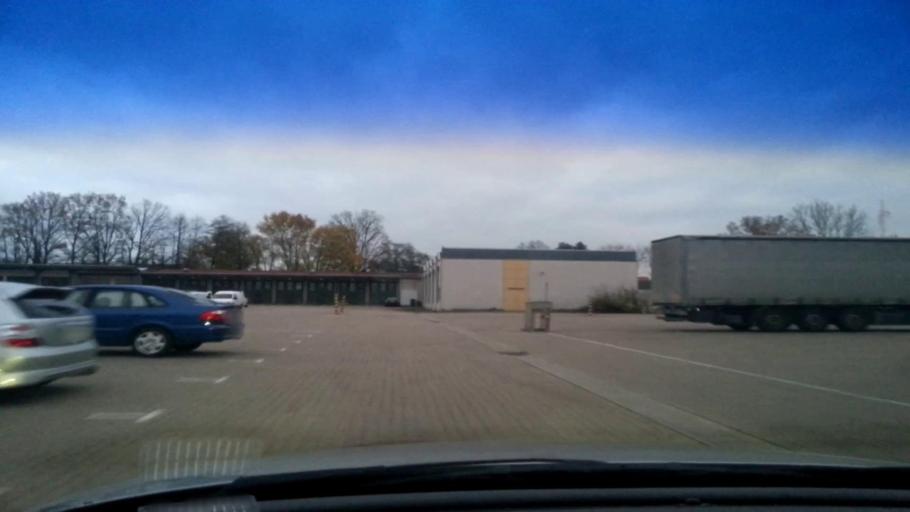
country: DE
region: Bavaria
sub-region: Upper Franconia
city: Gundelsheim
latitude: 49.9184
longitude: 10.9179
